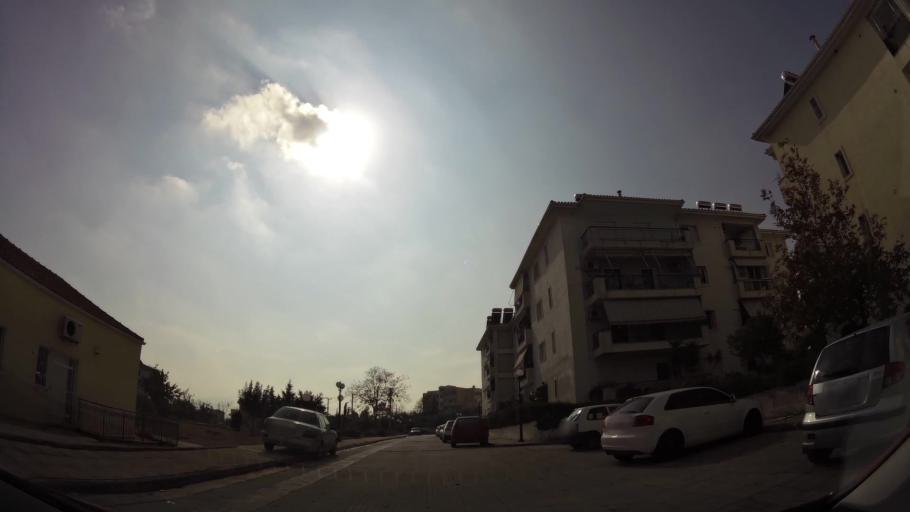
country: GR
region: Attica
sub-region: Nomarchia Dytikis Attikis
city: Zefyri
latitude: 38.0637
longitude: 23.7261
